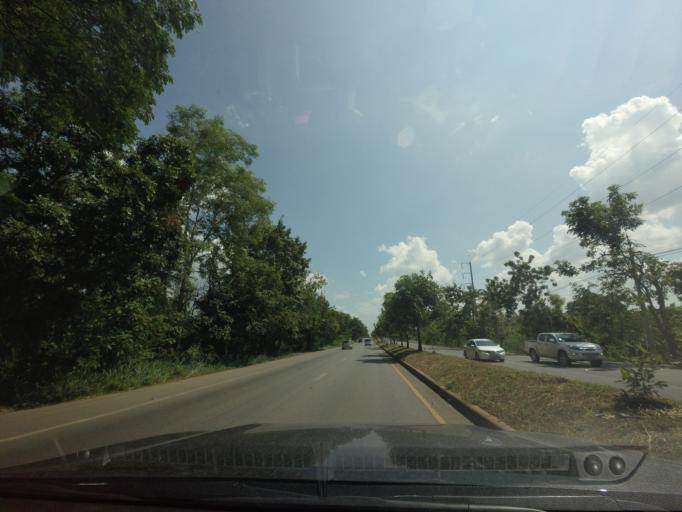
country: TH
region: Phetchabun
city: Nong Phai
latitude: 16.0632
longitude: 101.0723
